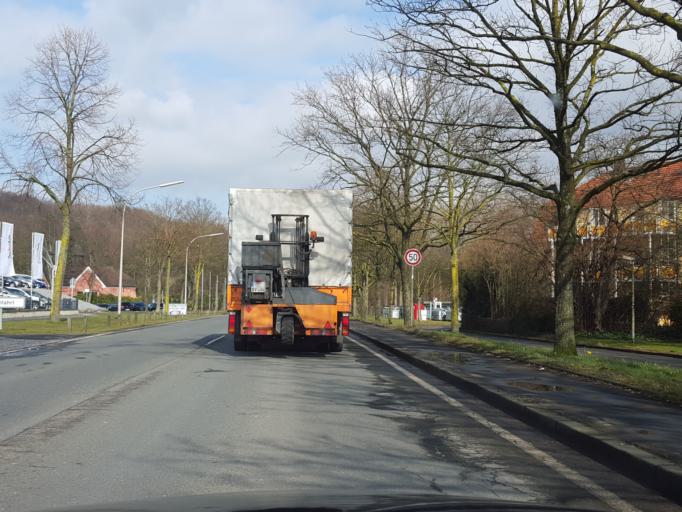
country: DE
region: North Rhine-Westphalia
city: Witten
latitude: 51.4512
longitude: 7.3668
